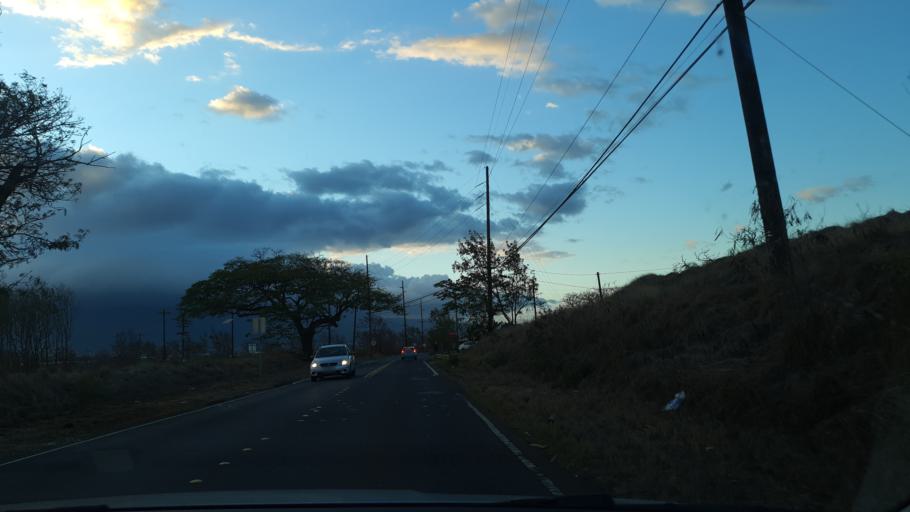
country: US
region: Hawaii
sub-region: Maui County
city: Kahului
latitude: 20.8720
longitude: -156.4389
